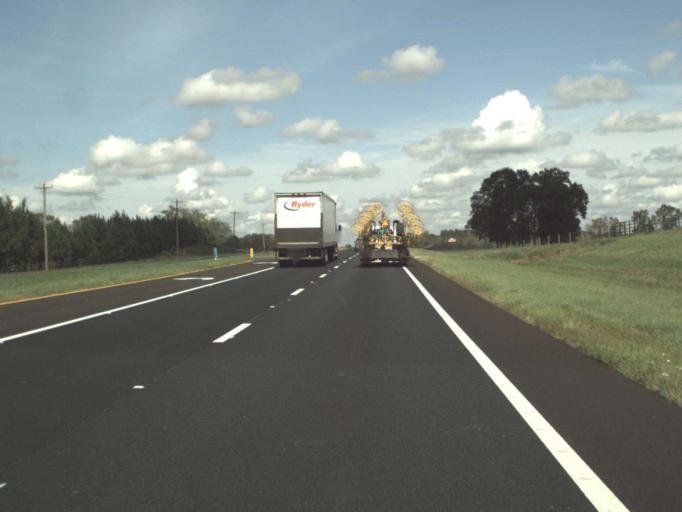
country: US
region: Florida
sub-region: Jackson County
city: Graceville
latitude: 30.9222
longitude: -85.3833
